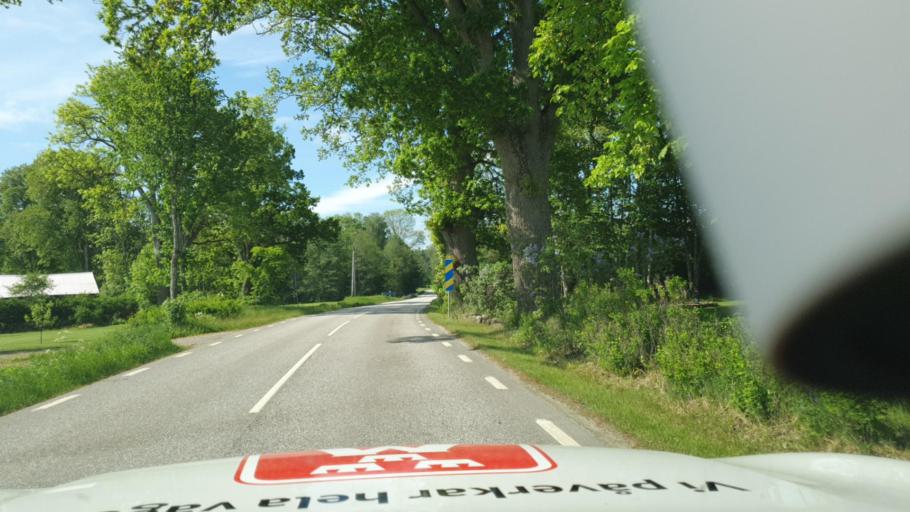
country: SE
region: Vaestra Goetaland
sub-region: Herrljunga Kommun
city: Herrljunga
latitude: 58.0418
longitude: 13.1897
